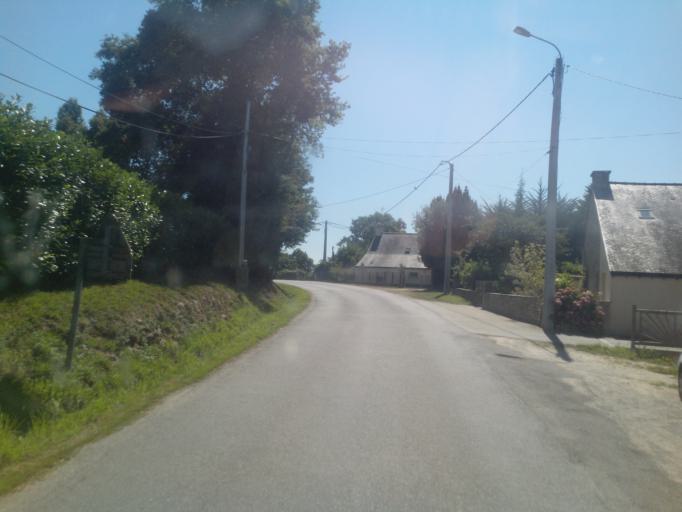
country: FR
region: Brittany
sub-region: Departement du Morbihan
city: Molac
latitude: 47.7330
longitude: -2.4384
